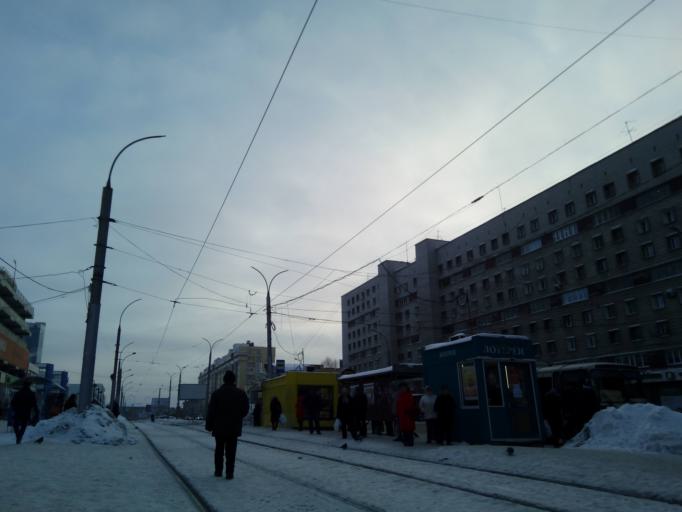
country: RU
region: Novosibirsk
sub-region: Novosibirskiy Rayon
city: Novosibirsk
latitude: 54.9824
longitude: 82.8905
